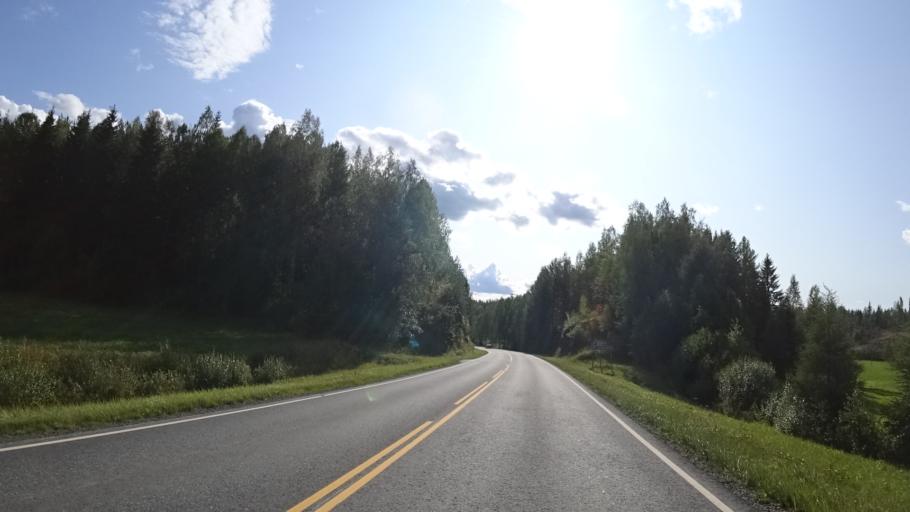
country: FI
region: North Karelia
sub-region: Keski-Karjala
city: Tohmajaervi
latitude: 62.2100
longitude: 30.2874
